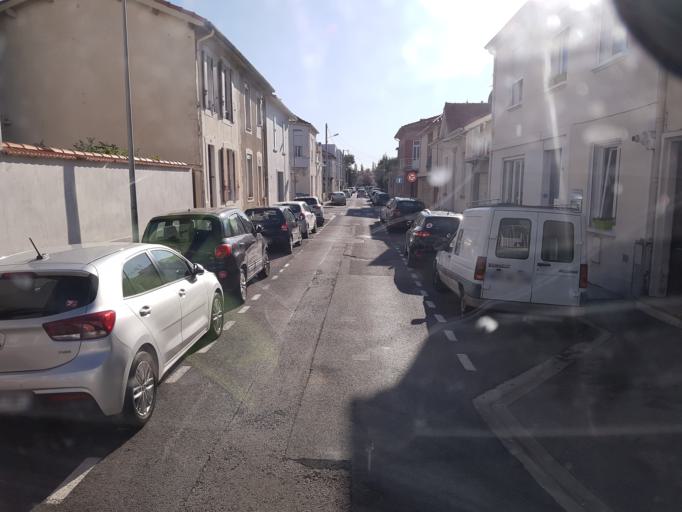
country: FR
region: Languedoc-Roussillon
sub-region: Departement de l'Aude
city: Narbonne
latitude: 43.1798
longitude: 3.0066
